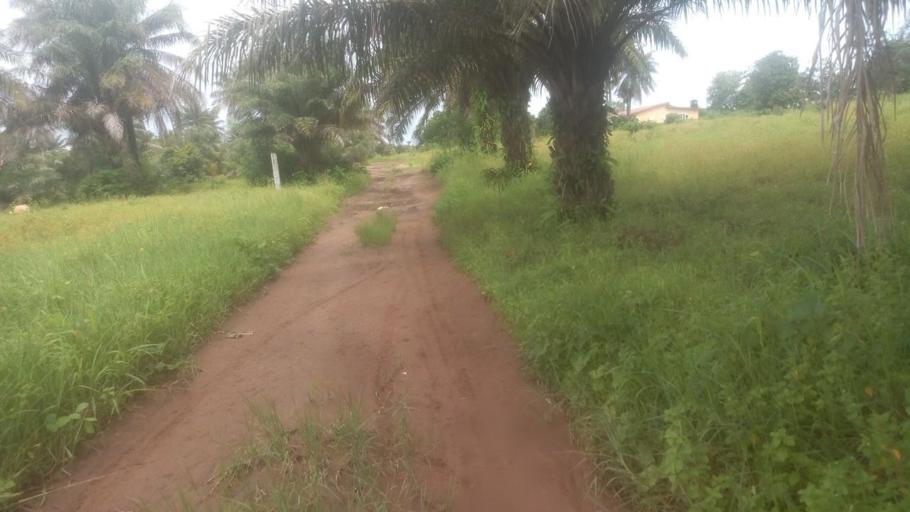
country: SL
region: Northern Province
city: Masoyila
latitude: 8.5940
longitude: -13.1857
